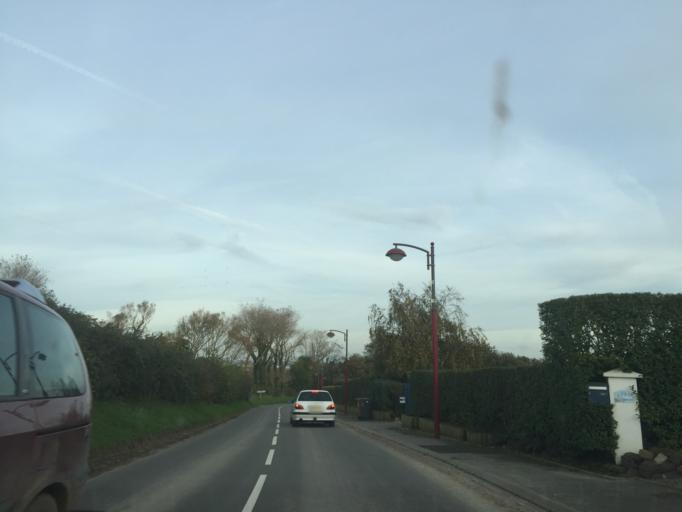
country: FR
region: Nord-Pas-de-Calais
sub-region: Departement du Pas-de-Calais
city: Sangatte
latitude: 50.9131
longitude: 1.7520
